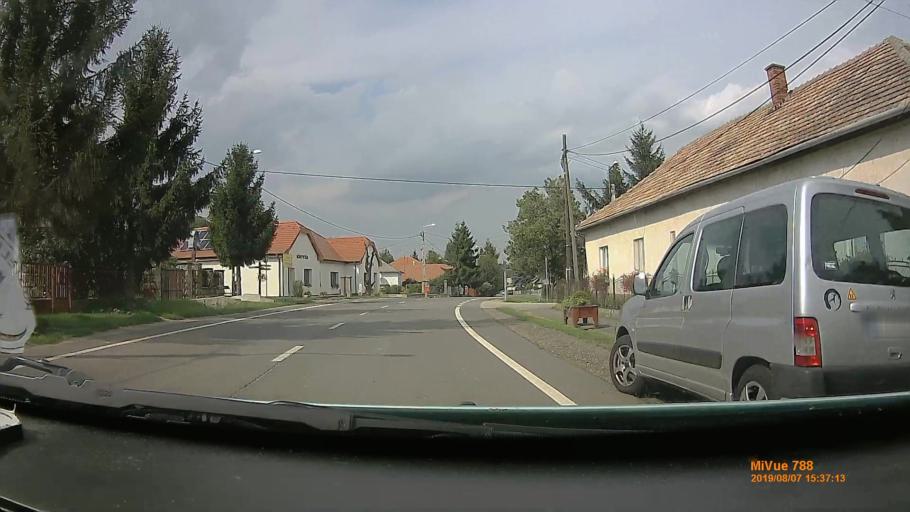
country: HU
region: Borsod-Abauj-Zemplen
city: Encs
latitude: 48.4173
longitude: 21.1741
